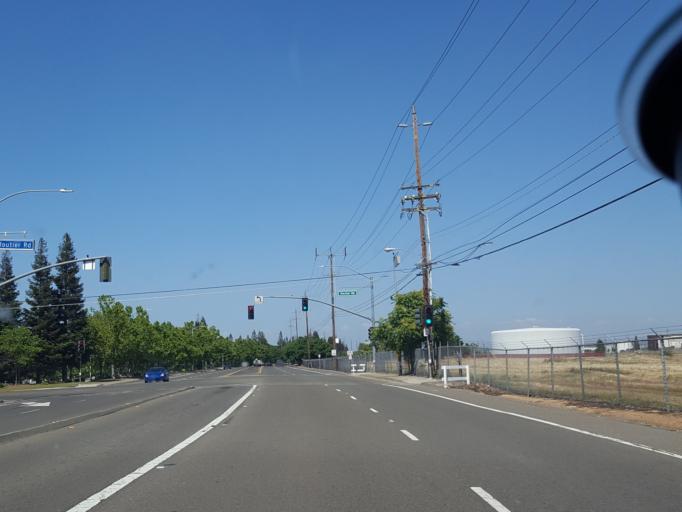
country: US
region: California
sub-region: Sacramento County
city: Rancho Cordova
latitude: 38.5607
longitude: -121.3178
